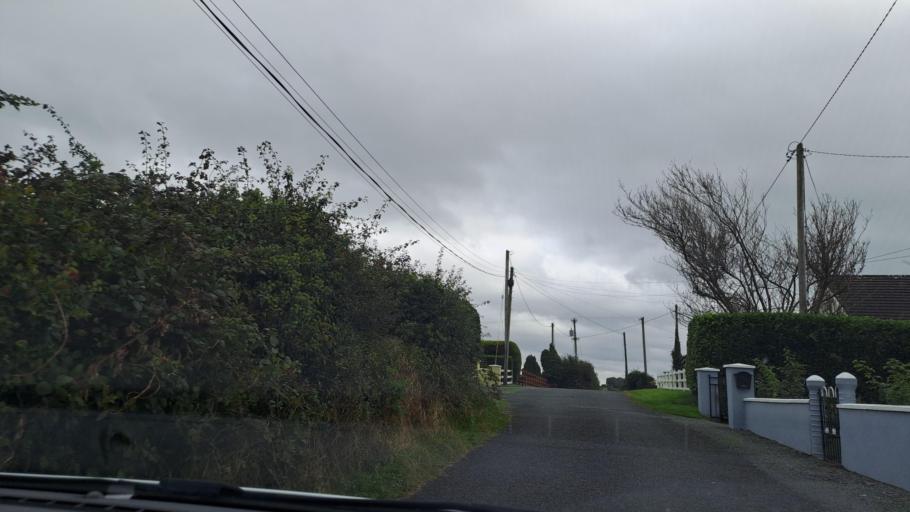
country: IE
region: Ulster
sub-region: An Cabhan
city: Bailieborough
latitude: 54.0011
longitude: -6.9023
